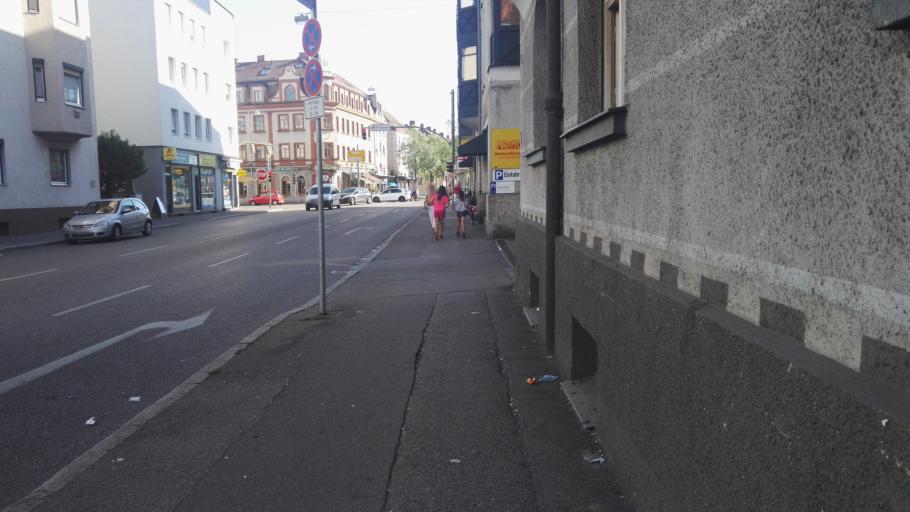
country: DE
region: Bavaria
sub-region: Swabia
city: Augsburg
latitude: 48.3820
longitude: 10.8745
